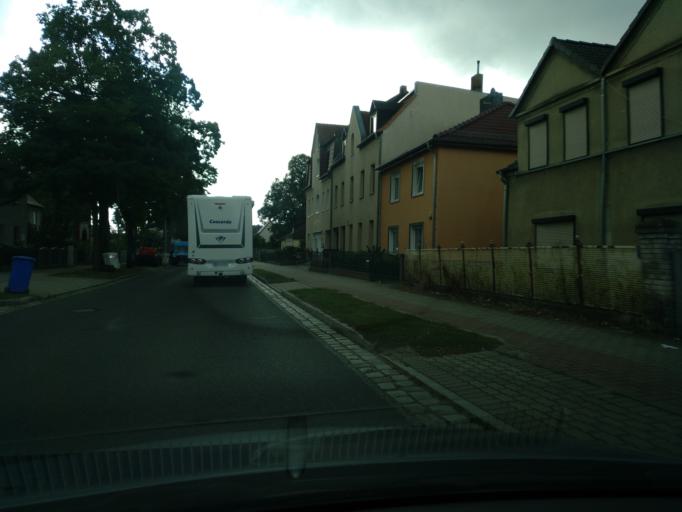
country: DE
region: Brandenburg
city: Woltersdorf
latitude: 52.4822
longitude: 13.7757
